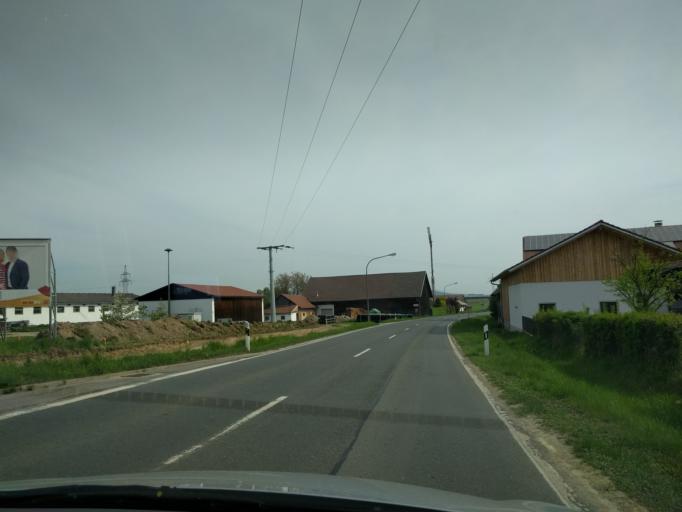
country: DE
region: Bavaria
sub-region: Upper Palatinate
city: Cham
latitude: 49.1921
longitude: 12.6445
